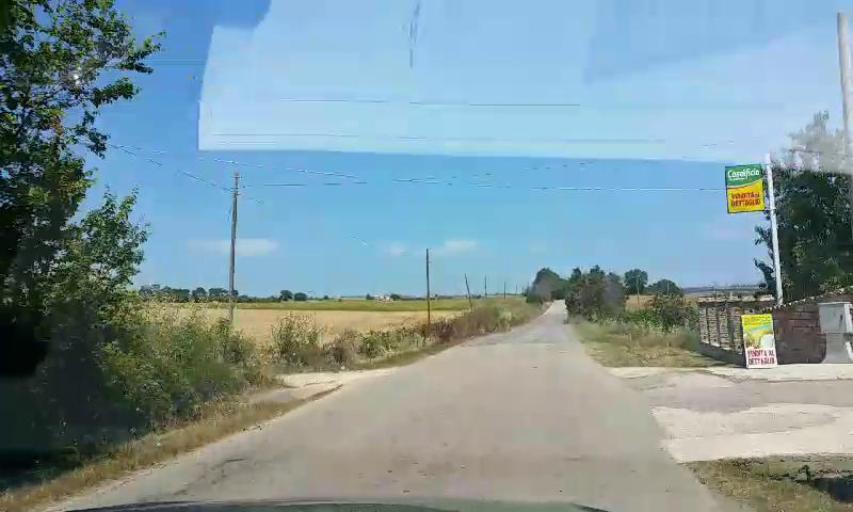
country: IT
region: Molise
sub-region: Provincia di Campobasso
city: Guglionesi
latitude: 41.9568
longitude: 14.9004
